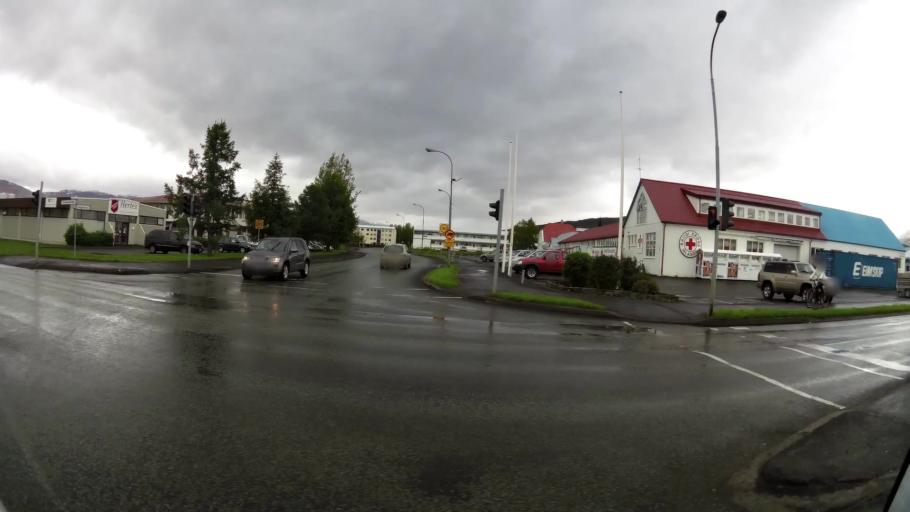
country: IS
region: Northeast
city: Akureyri
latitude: 65.6777
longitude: -18.1235
